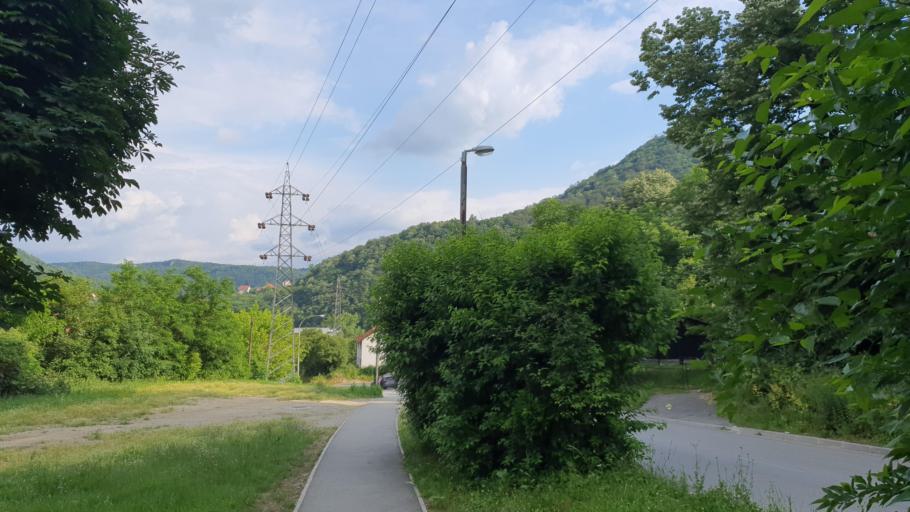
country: RS
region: Central Serbia
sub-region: Zlatiborski Okrug
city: Uzice
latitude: 43.8508
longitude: 19.8512
